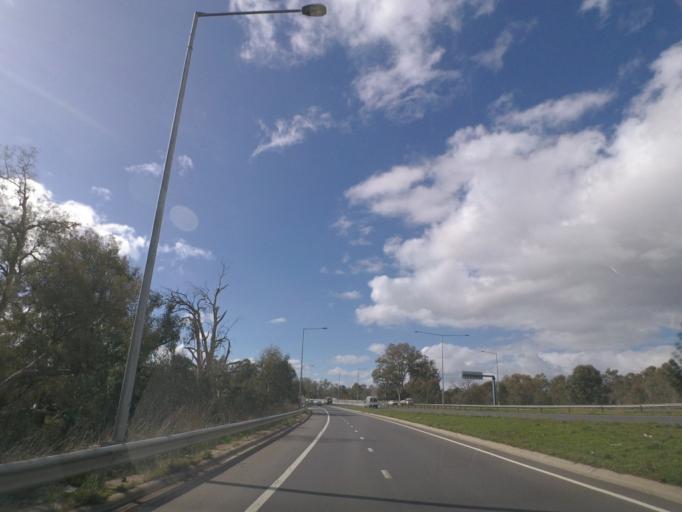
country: AU
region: Victoria
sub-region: Wodonga
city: Wodonga
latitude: -36.1078
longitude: 146.9023
